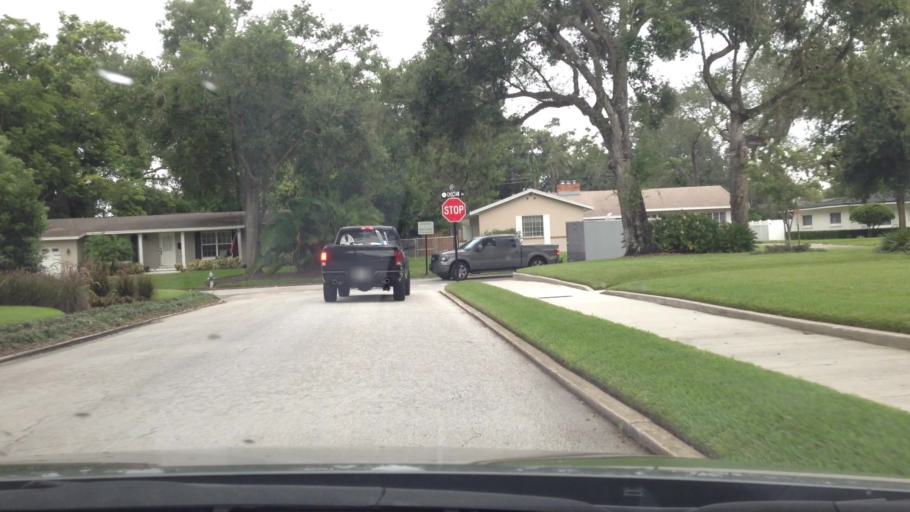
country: US
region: Florida
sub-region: Orange County
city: Maitland
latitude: 28.6322
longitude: -81.3464
